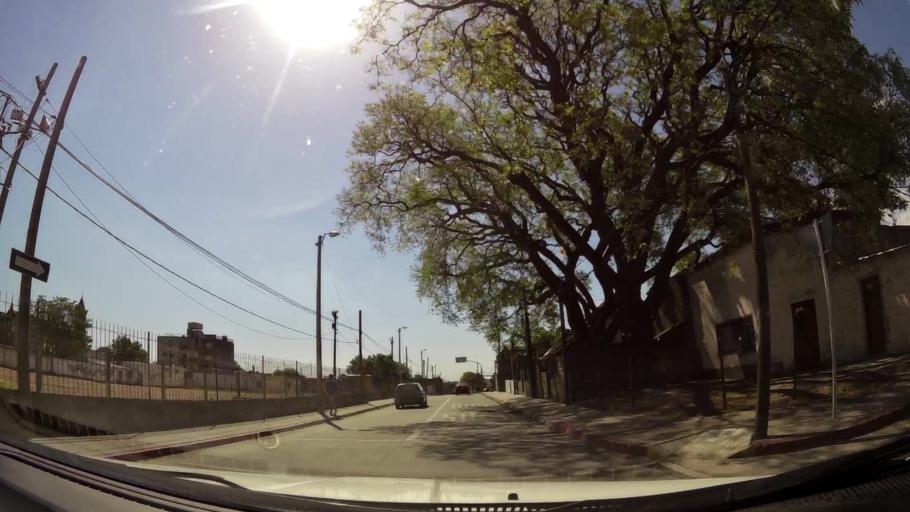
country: UY
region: Montevideo
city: Montevideo
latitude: -34.8512
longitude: -56.2268
